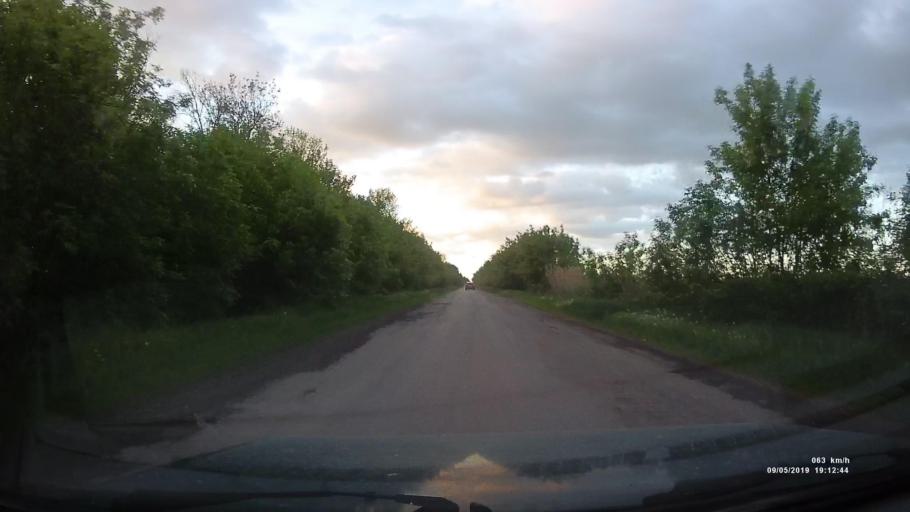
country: RU
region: Krasnodarskiy
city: Kanelovskaya
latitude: 46.7443
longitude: 39.2137
